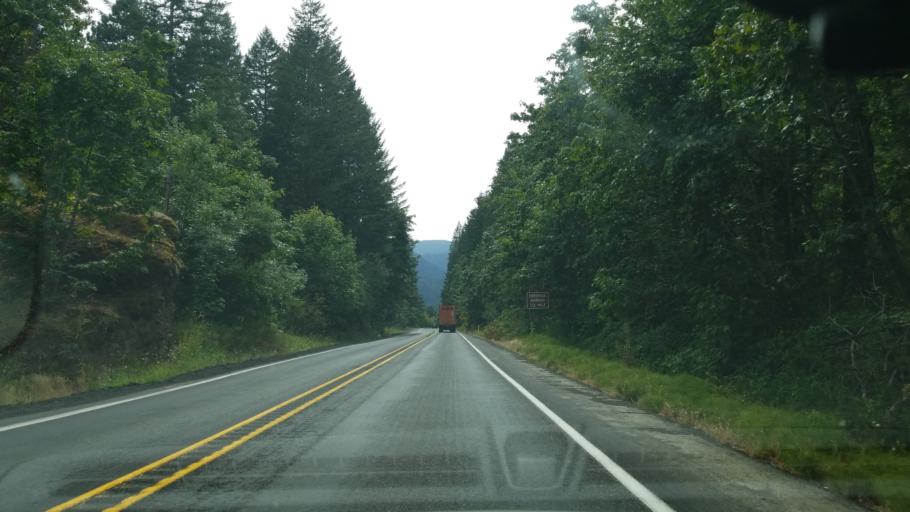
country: US
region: Oregon
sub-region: Hood River County
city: Cascade Locks
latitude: 45.6569
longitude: -121.9096
